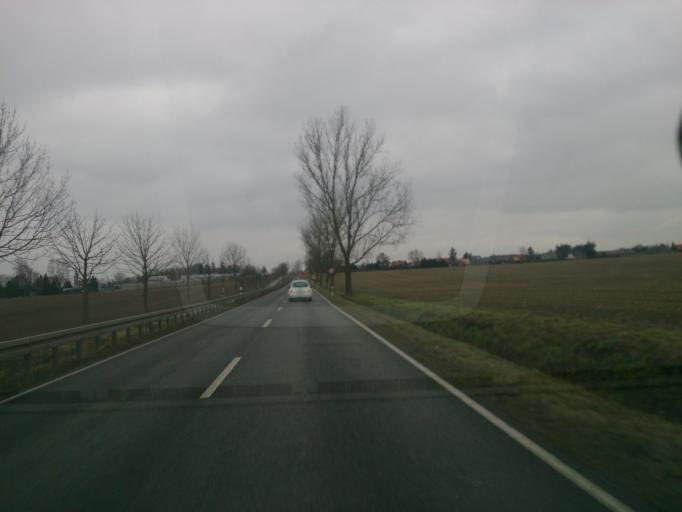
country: DE
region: Mecklenburg-Vorpommern
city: Demmin
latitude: 53.8867
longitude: 13.0300
